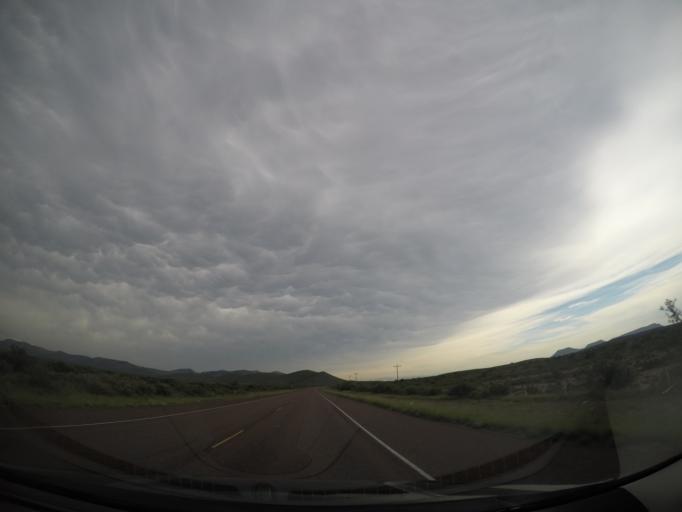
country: US
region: Texas
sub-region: Terrell County
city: Sanderson
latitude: 30.2171
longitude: -103.0150
